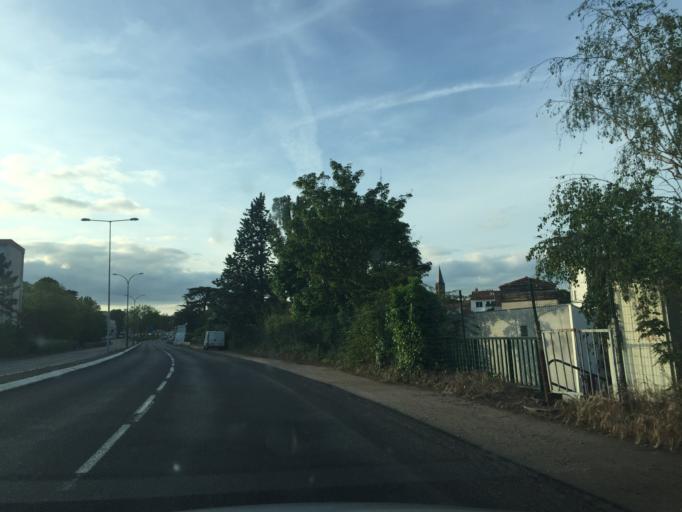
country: FR
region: Auvergne
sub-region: Departement du Puy-de-Dome
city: Riom
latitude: 45.8887
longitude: 3.1116
